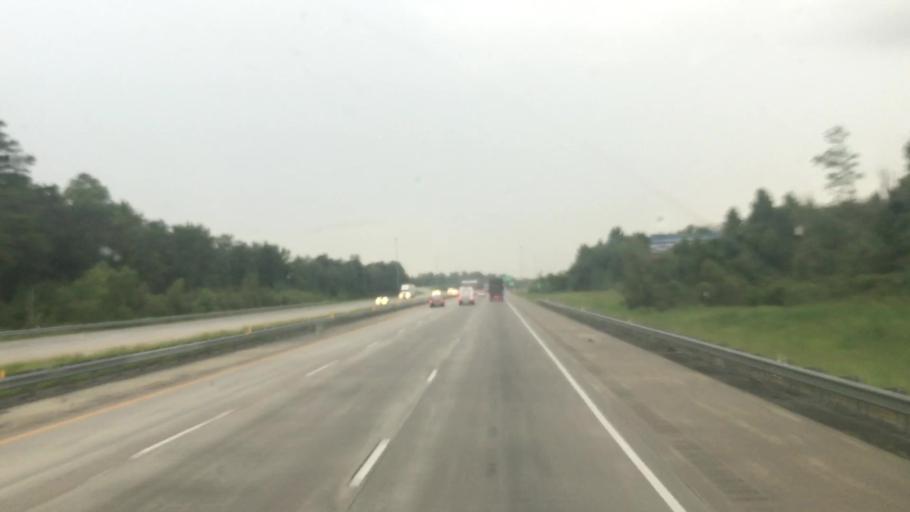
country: US
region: Georgia
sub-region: Dooly County
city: Unadilla
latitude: 32.1983
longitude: -83.7472
